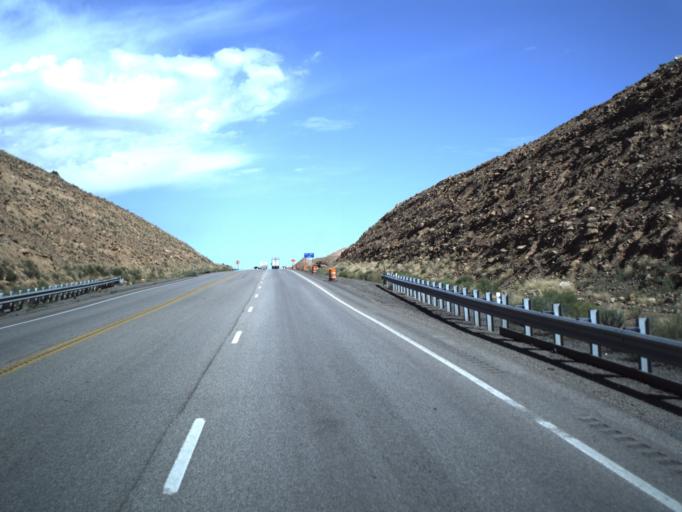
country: US
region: Utah
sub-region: Carbon County
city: East Carbon City
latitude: 39.3954
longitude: -110.4188
